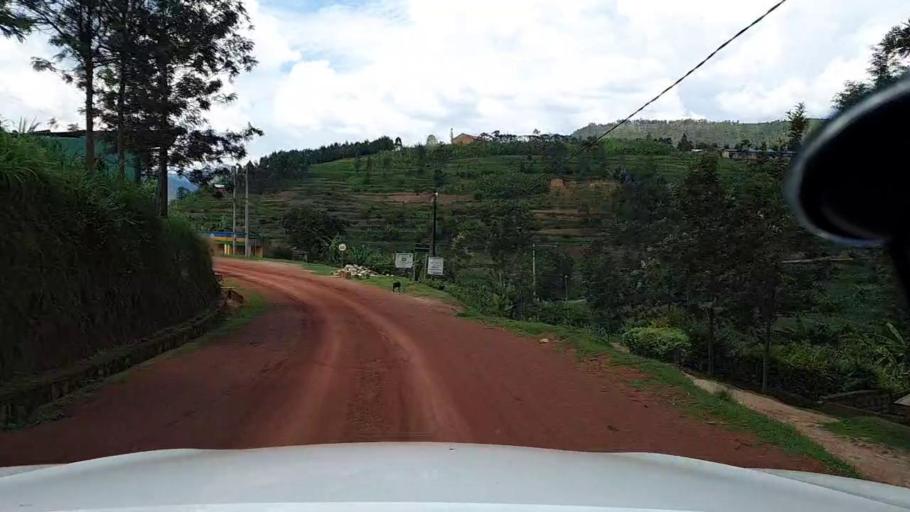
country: RW
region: Northern Province
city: Musanze
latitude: -1.6900
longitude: 29.8223
